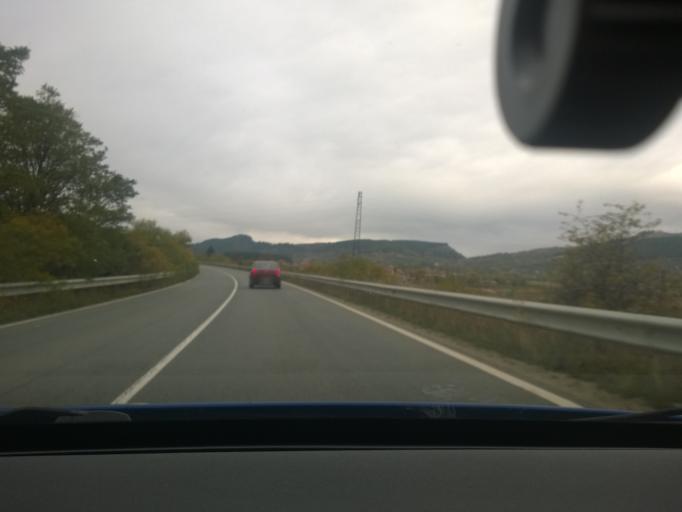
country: BG
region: Sofiya
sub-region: Obshtina Dragoman
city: Dragoman
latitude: 42.9283
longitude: 22.9345
